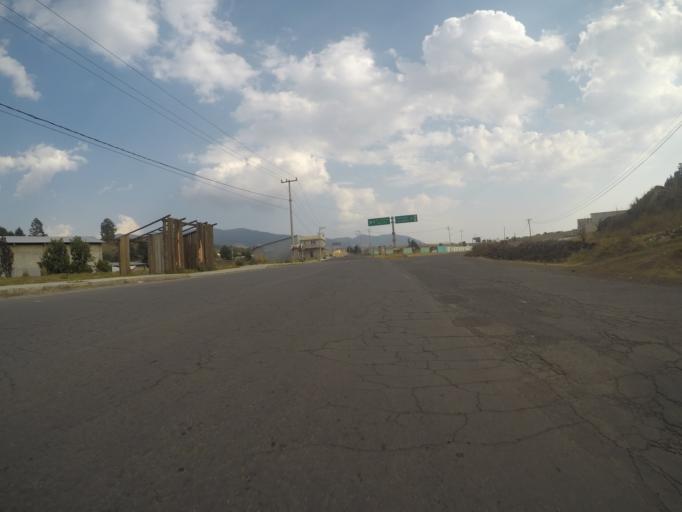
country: MX
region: Mexico
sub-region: Xalatlaco
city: El Aguila (La Mesa)
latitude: 19.1661
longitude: -99.4079
